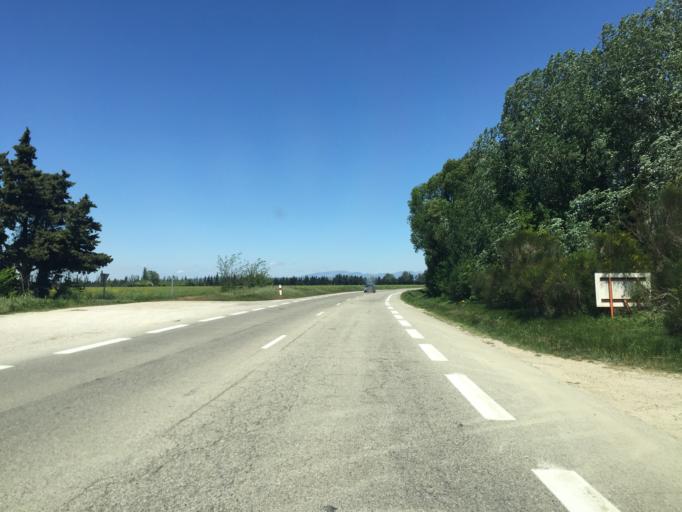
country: FR
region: Provence-Alpes-Cote d'Azur
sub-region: Departement du Vaucluse
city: Jonquieres
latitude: 44.1178
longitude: 4.9267
